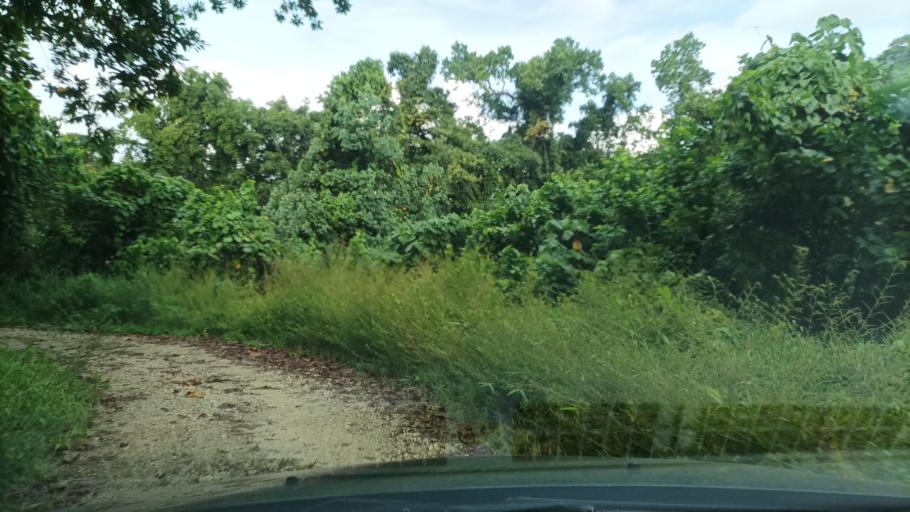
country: FM
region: Kosrae
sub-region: Utwe Municipality
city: Utwe
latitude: 5.2749
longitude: 162.9521
